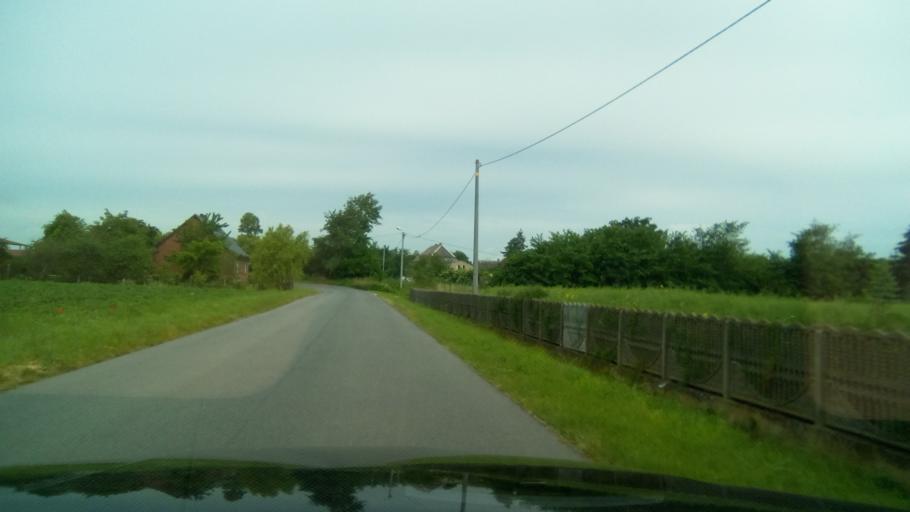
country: PL
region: Greater Poland Voivodeship
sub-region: Powiat gnieznienski
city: Mieleszyn
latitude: 52.6919
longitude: 17.5181
